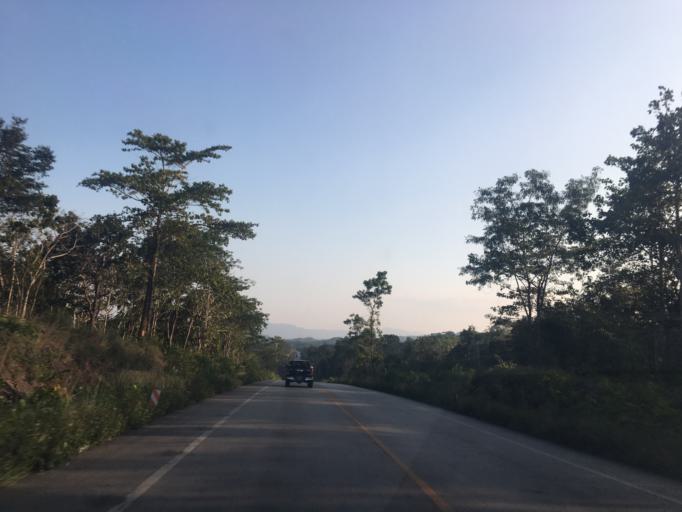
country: TH
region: Lampang
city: Ngao
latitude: 18.6939
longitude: 100.0023
